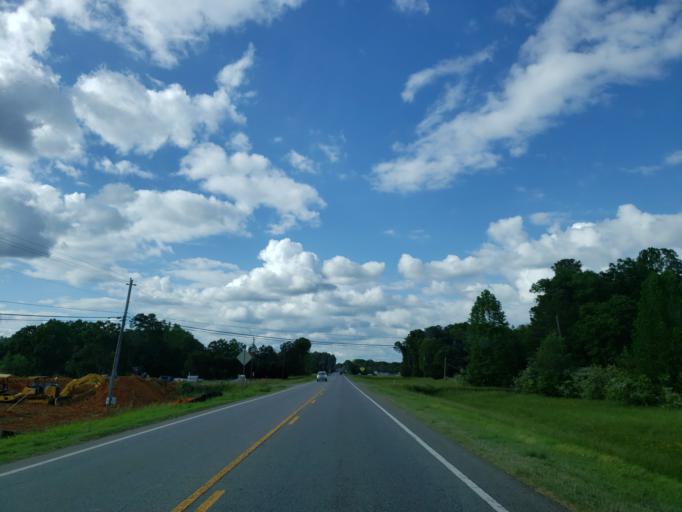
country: US
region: Georgia
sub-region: Bartow County
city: Cartersville
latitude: 34.2371
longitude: -84.8566
